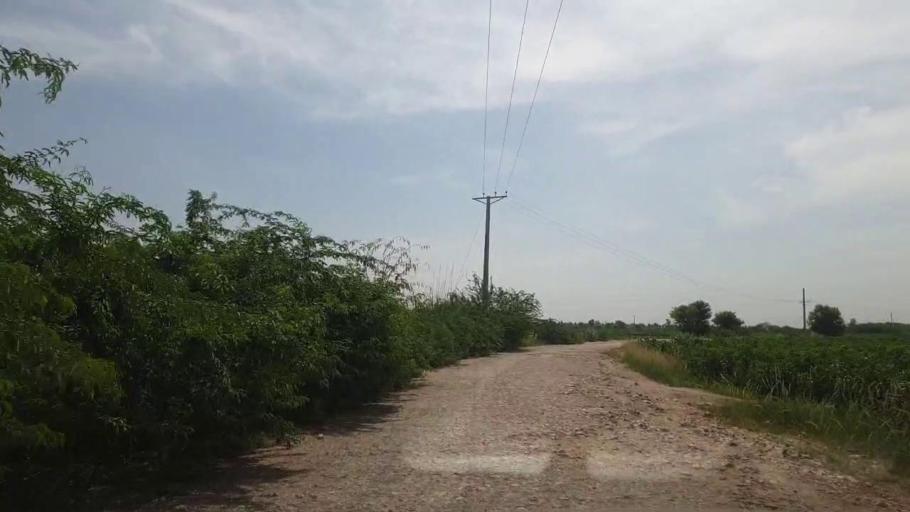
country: PK
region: Sindh
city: Kot Diji
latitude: 27.1289
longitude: 68.9971
